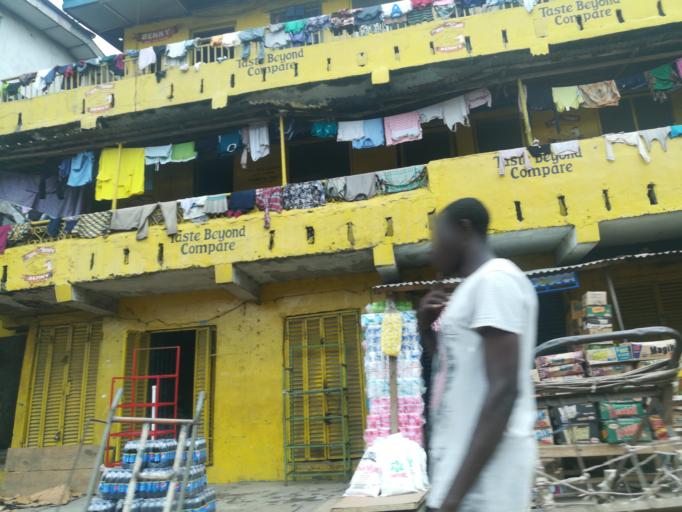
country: NG
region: Lagos
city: Mushin
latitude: 6.5295
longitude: 3.3569
